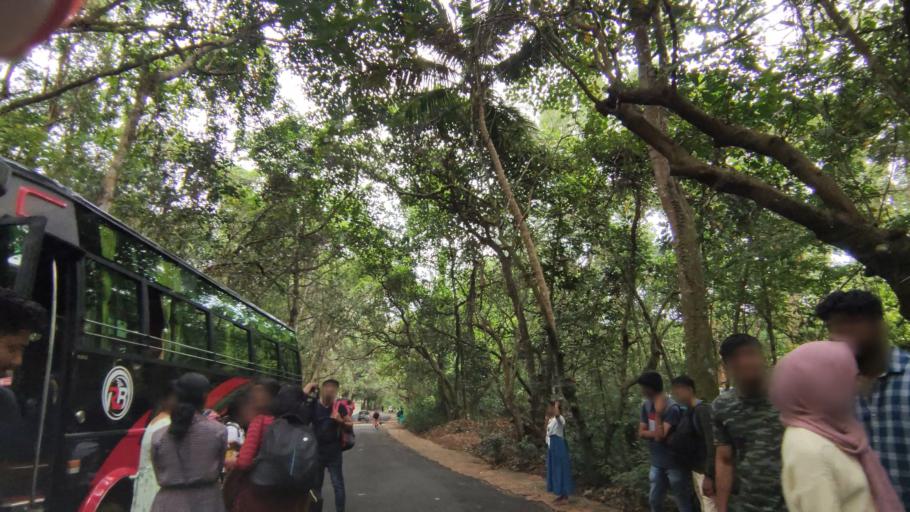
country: IN
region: Kerala
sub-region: Kottayam
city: Kottayam
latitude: 9.6598
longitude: 76.5334
